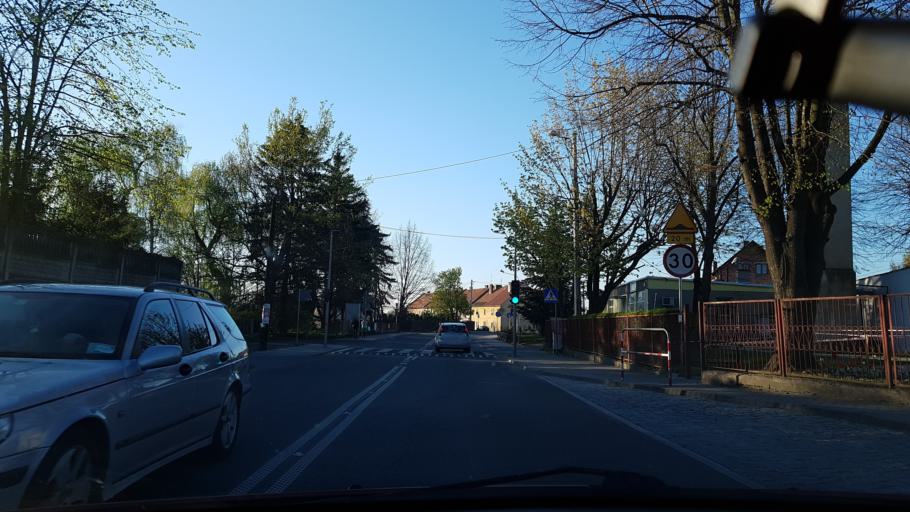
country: PL
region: Opole Voivodeship
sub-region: Powiat nyski
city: Nysa
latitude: 50.4339
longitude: 17.3058
